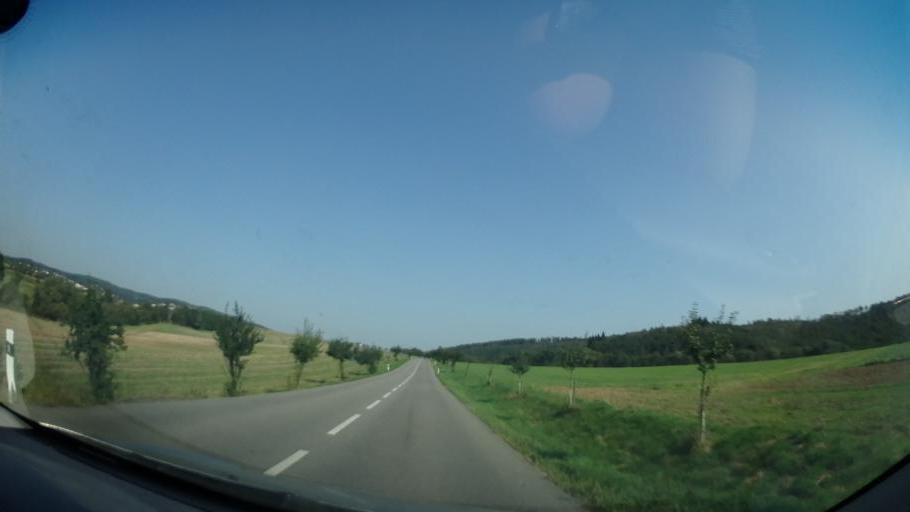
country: CZ
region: South Moravian
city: Kurim
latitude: 49.2423
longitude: 16.5303
